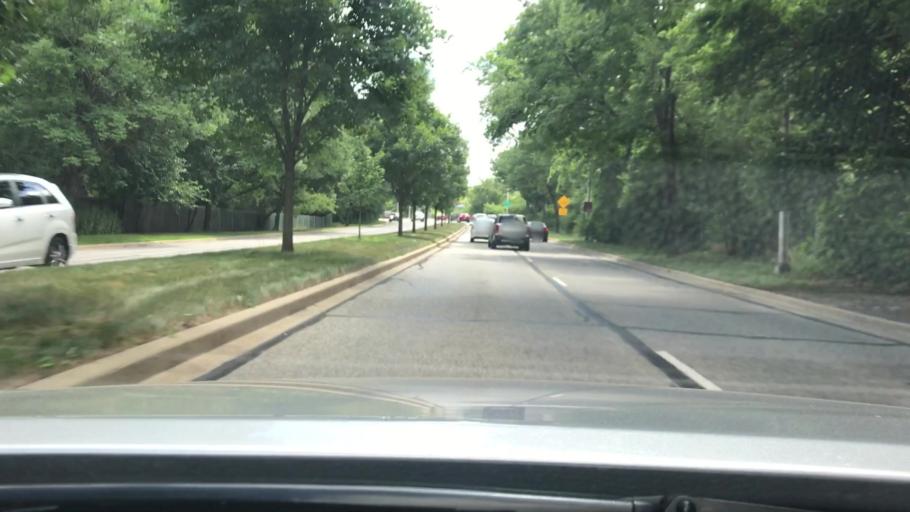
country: US
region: Illinois
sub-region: DuPage County
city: Naperville
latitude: 41.7941
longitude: -88.1189
